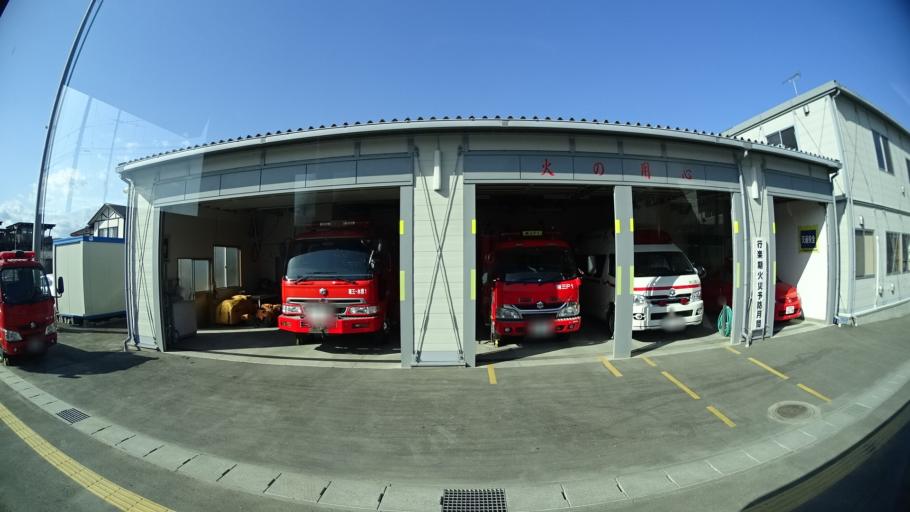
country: JP
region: Miyagi
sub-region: Oshika Gun
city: Onagawa Cho
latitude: 38.6818
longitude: 141.4614
